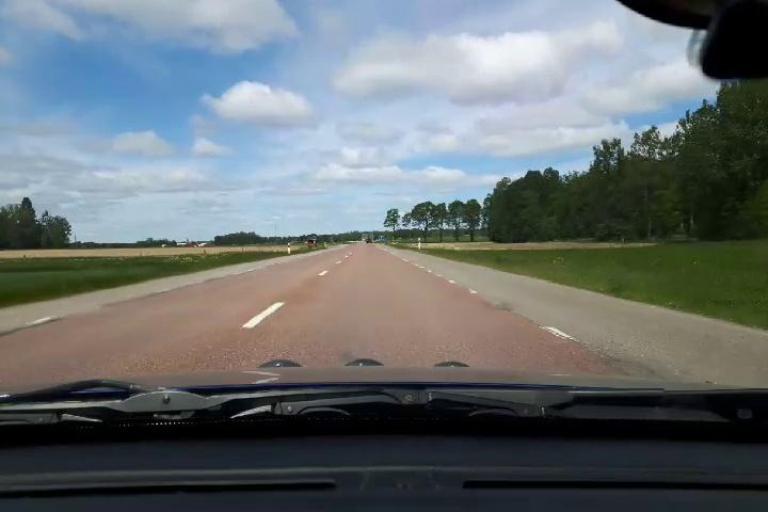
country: SE
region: Uppsala
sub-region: Osthammars Kommun
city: Bjorklinge
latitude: 60.0111
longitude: 17.5598
